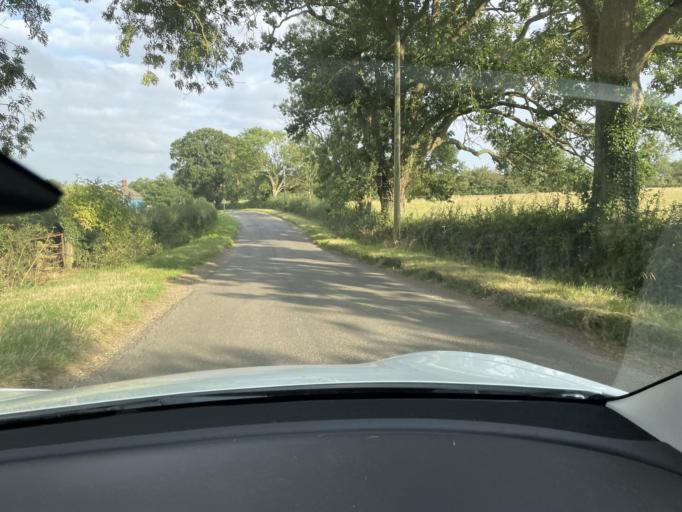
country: GB
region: England
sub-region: Northamptonshire
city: Brixworth
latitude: 52.3916
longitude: -0.9622
